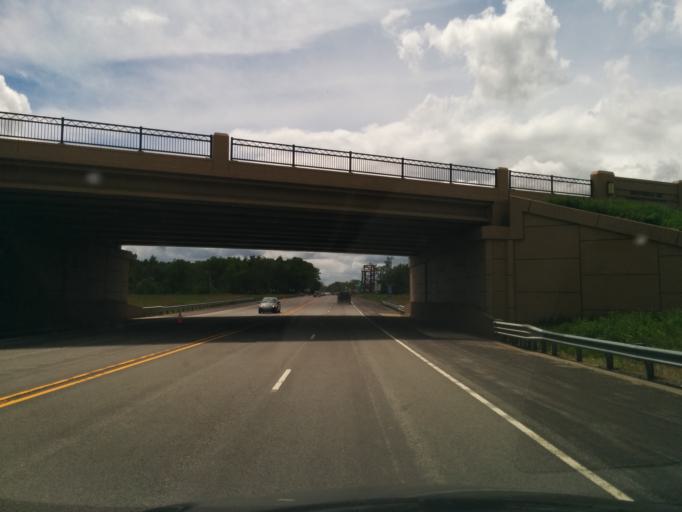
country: US
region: Indiana
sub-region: Porter County
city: Porter
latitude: 41.6356
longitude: -87.0582
